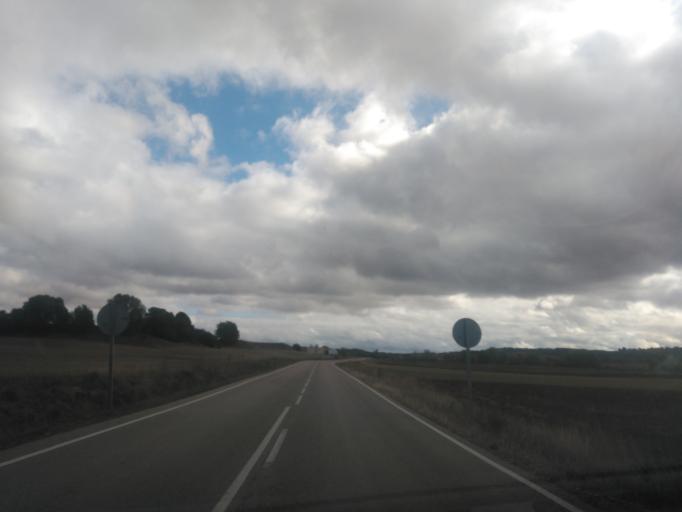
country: ES
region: Castille and Leon
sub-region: Provincia de Soria
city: Alcubilla de Avellaneda
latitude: 41.7227
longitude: -3.3225
